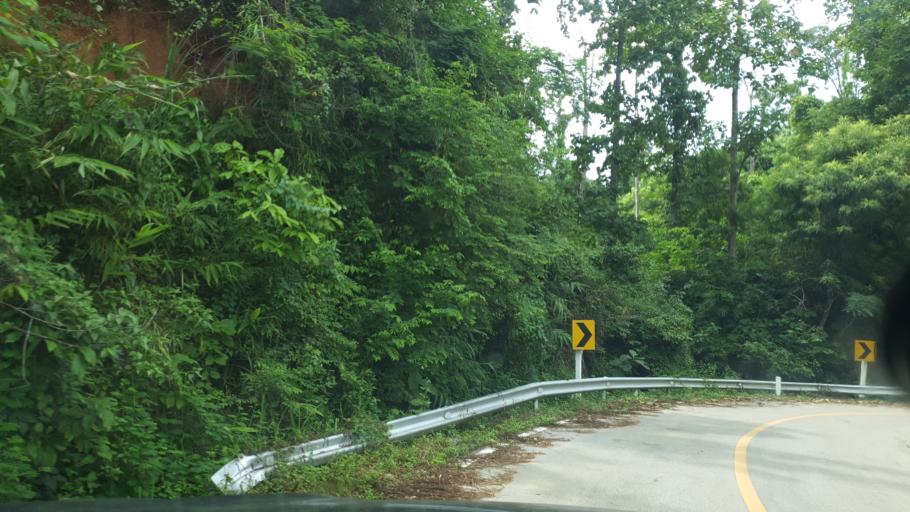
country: TH
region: Lampang
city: Hang Chat
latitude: 18.3641
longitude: 99.2603
